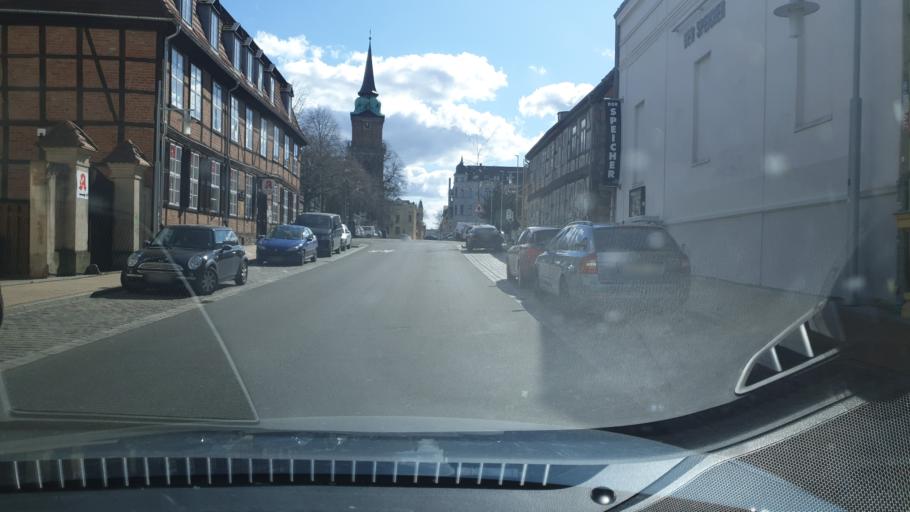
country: DE
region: Mecklenburg-Vorpommern
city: Schelfstadt
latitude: 53.6341
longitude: 11.4180
